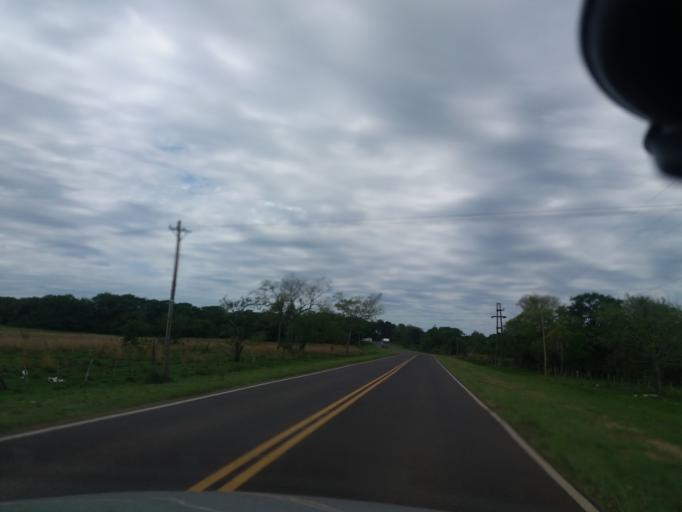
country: AR
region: Corrientes
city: Riachuelo
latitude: -27.4567
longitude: -58.6985
